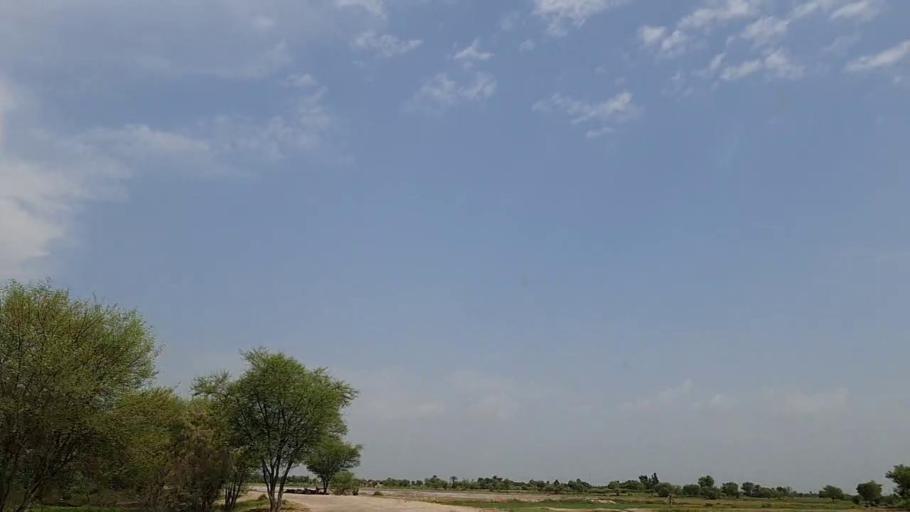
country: PK
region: Sindh
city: Khanpur
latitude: 27.8382
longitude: 69.4697
